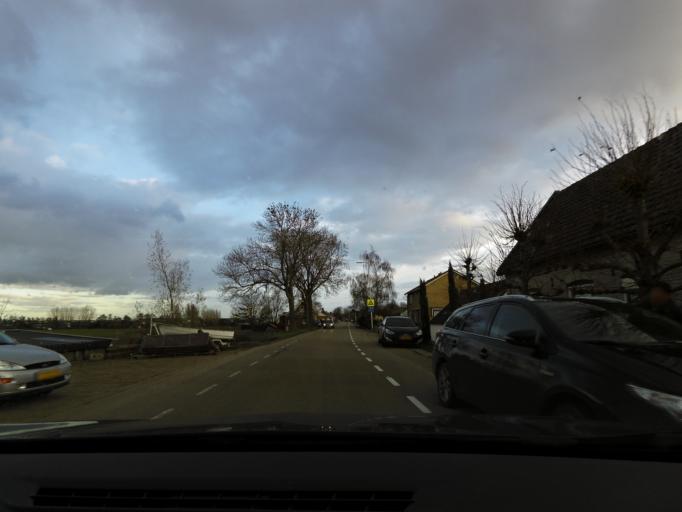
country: NL
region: South Holland
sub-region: Gemeente Binnenmaas
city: Mijnsheerenland
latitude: 51.8130
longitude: 4.5125
